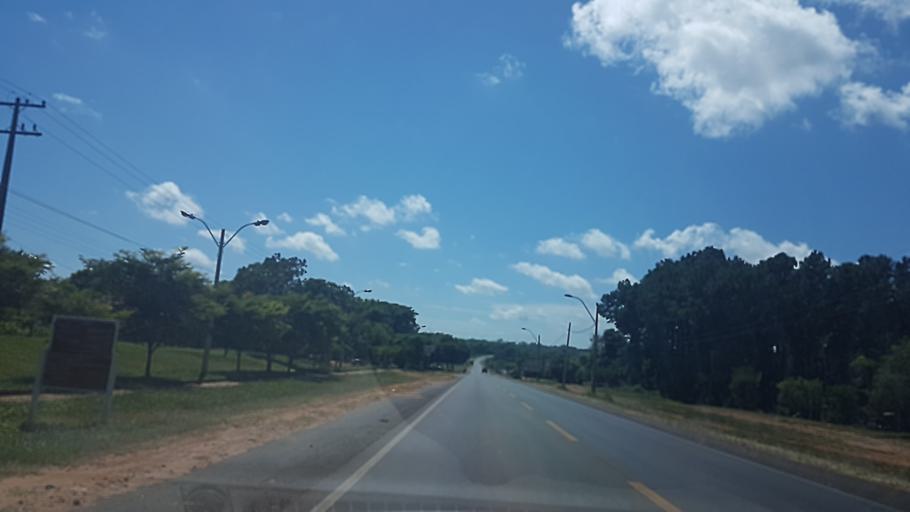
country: PY
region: Misiones
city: San Juan Bautista
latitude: -26.6735
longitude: -57.1155
